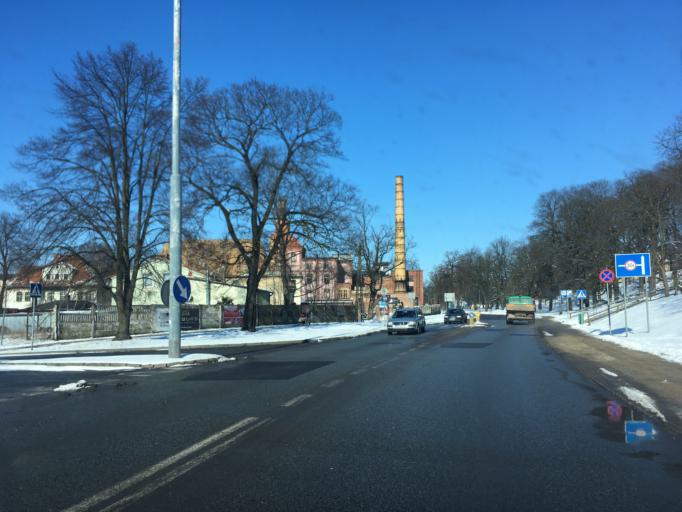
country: PL
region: Pomeranian Voivodeship
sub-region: Slupsk
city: Slupsk
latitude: 54.4705
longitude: 17.0394
